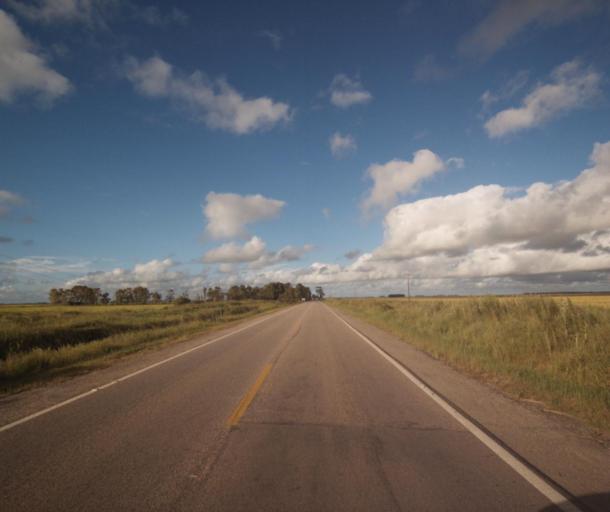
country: BR
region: Rio Grande do Sul
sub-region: Rio Grande
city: Rio Grande
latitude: -32.2082
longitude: -52.4521
